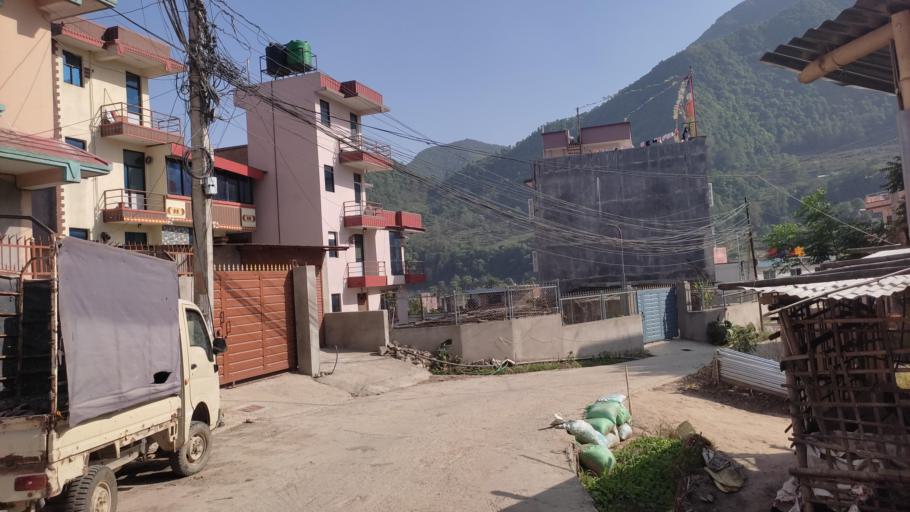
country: NP
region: Central Region
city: Kirtipur
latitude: 27.6644
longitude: 85.2655
